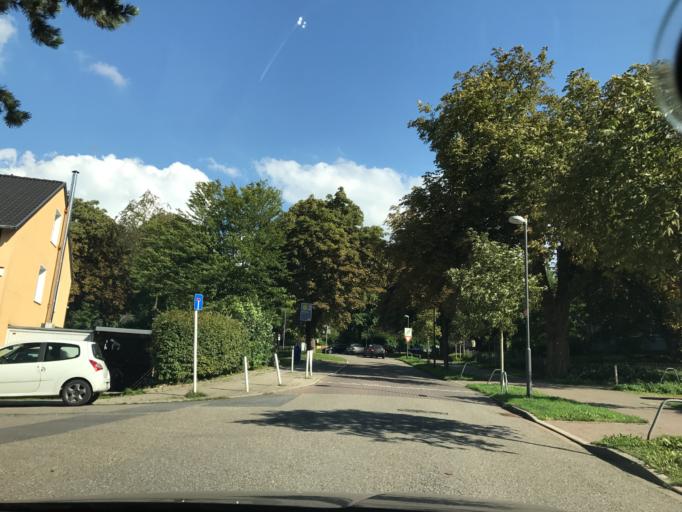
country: DE
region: North Rhine-Westphalia
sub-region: Regierungsbezirk Dusseldorf
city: Velbert
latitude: 51.3756
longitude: 7.0145
